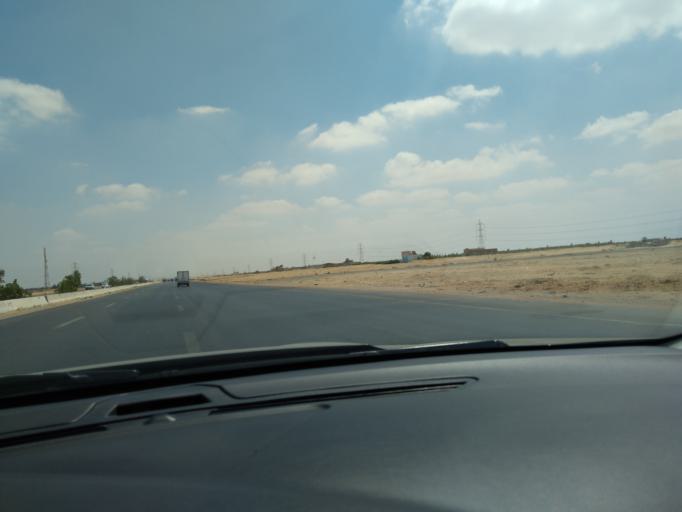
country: EG
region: Al Isma'iliyah
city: At Tall al Kabir
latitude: 30.3497
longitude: 31.8827
